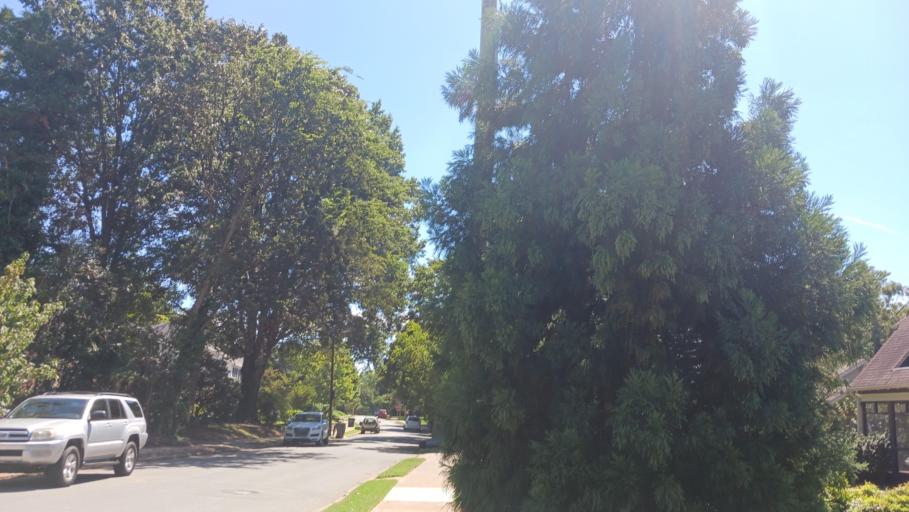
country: US
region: North Carolina
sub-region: Mecklenburg County
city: Charlotte
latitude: 35.2106
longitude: -80.8176
